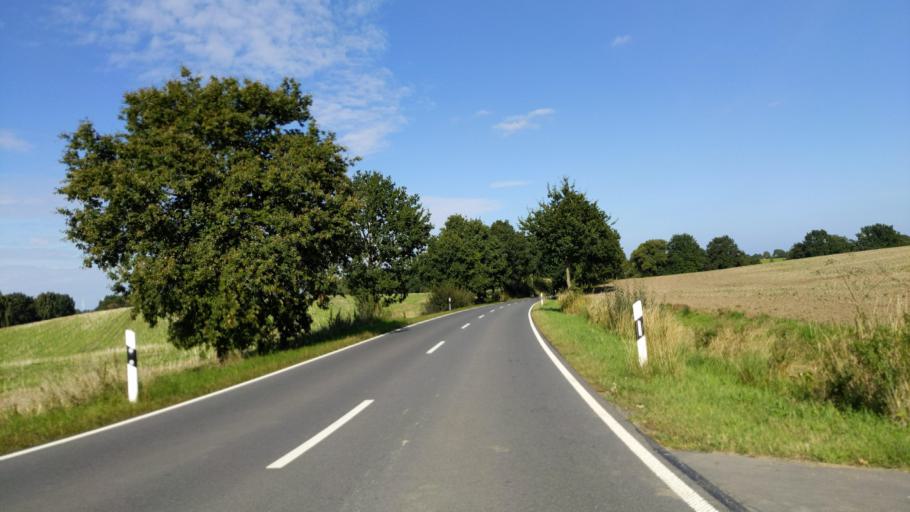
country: DE
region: Schleswig-Holstein
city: Stockelsdorf
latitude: 53.9609
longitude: 10.6359
